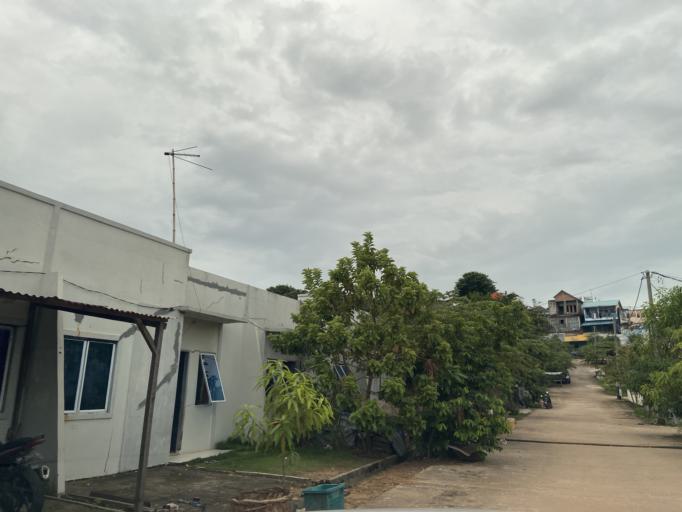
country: SG
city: Singapore
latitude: 1.1671
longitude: 104.0204
